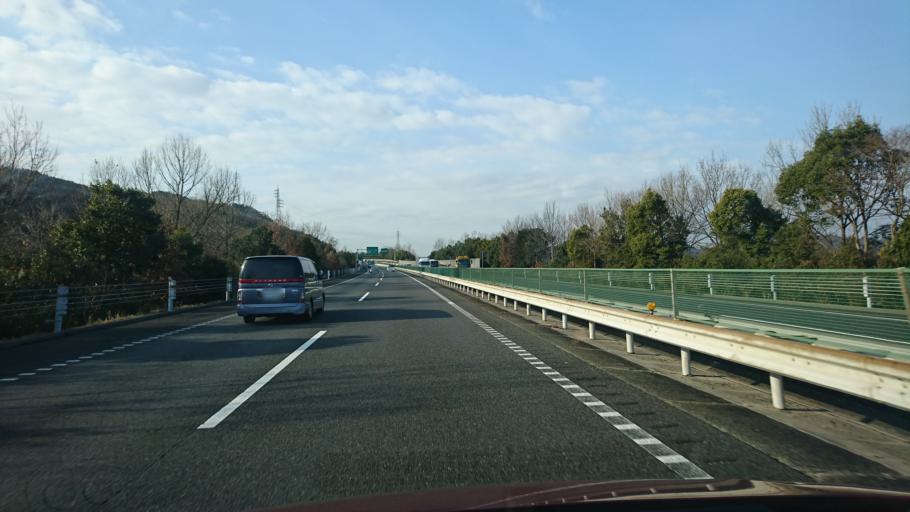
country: JP
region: Hyogo
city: Tatsunocho-tominaga
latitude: 34.8430
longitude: 134.5164
